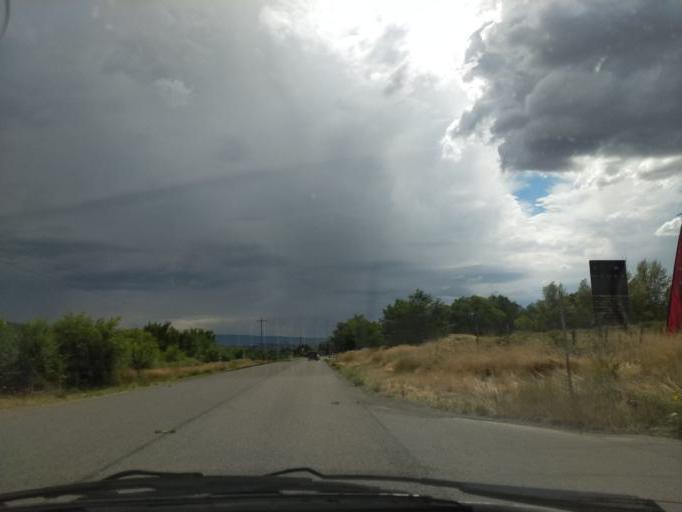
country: US
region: Colorado
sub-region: Delta County
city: Paonia
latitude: 38.8835
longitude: -107.5908
